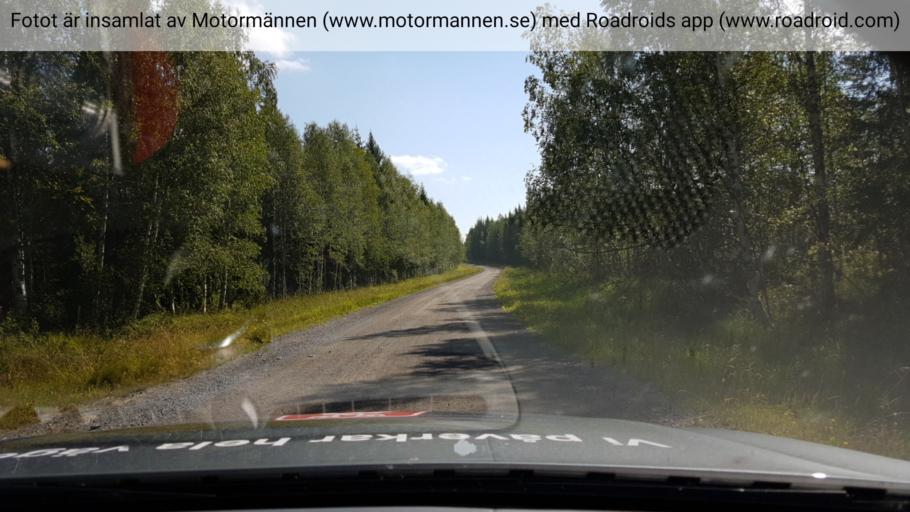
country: SE
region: Jaemtland
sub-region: Stroemsunds Kommun
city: Stroemsund
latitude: 63.3444
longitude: 15.3898
